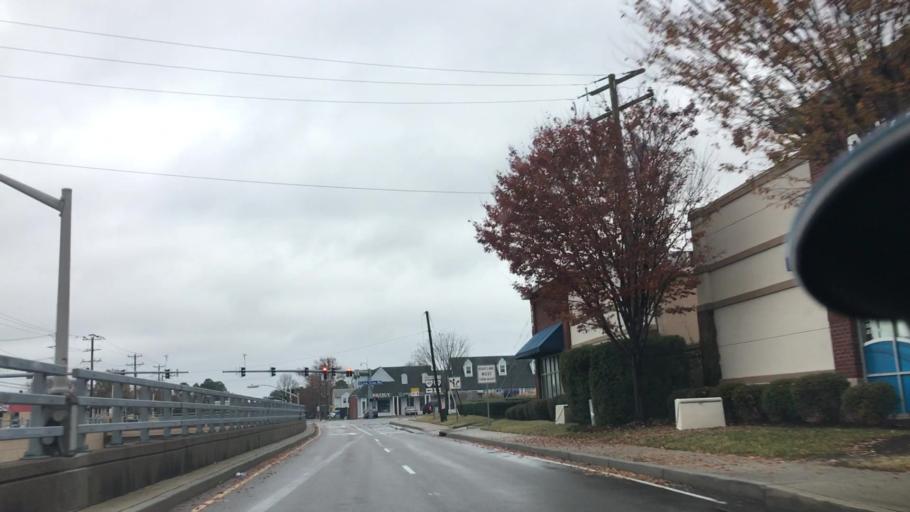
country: US
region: Virginia
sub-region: City of Norfolk
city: Norfolk
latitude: 36.9153
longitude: -76.2541
